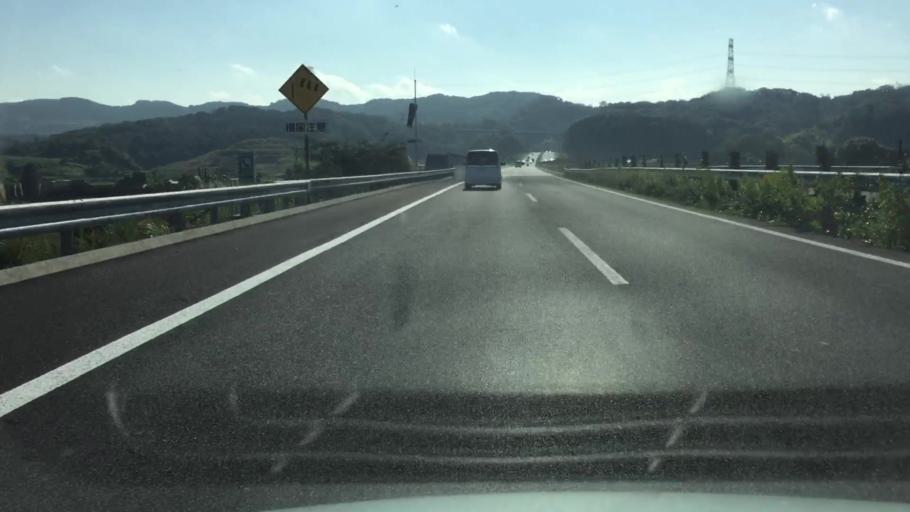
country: JP
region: Tochigi
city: Mooka
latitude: 36.3871
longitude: 140.0231
